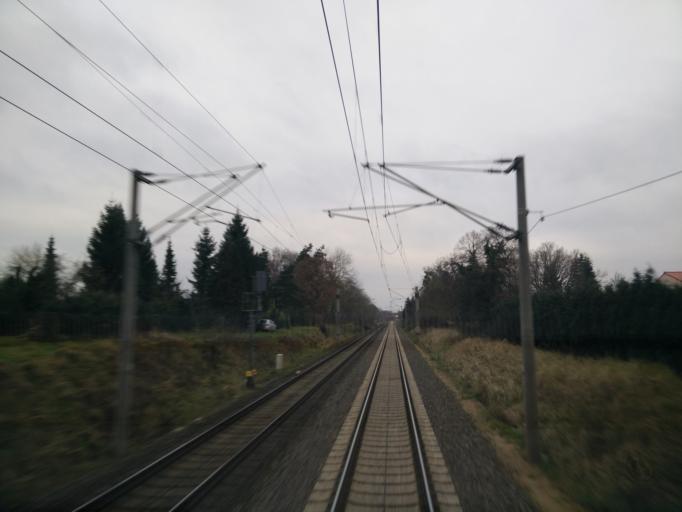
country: DE
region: Mecklenburg-Vorpommern
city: Grabow
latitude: 53.2741
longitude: 11.5813
